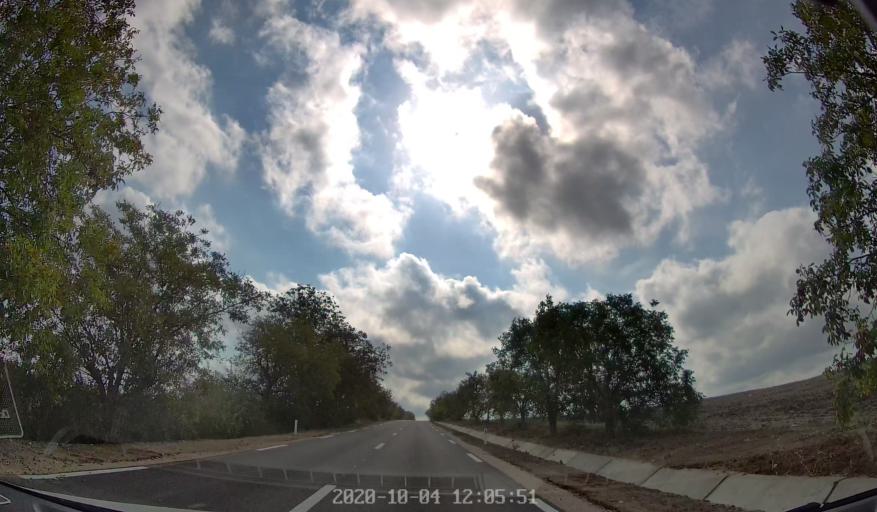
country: MD
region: Rezina
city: Saharna
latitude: 47.5897
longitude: 28.9533
